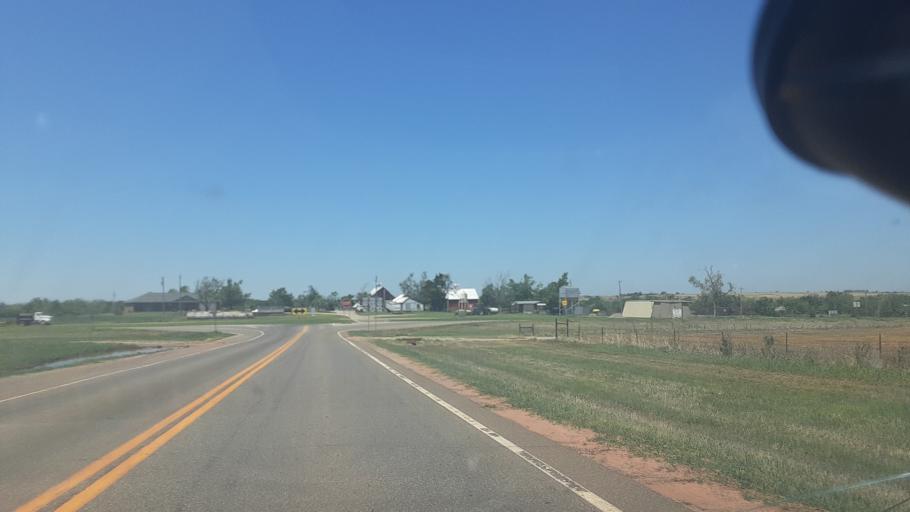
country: US
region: Oklahoma
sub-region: Noble County
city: Perry
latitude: 36.1110
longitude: -97.3874
